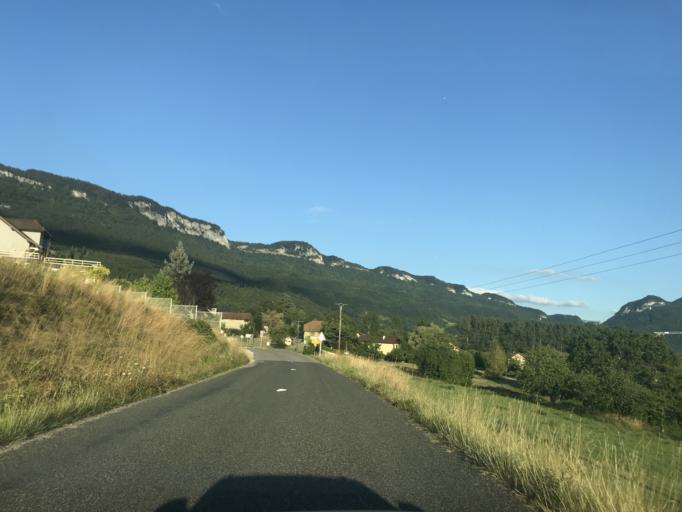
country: FR
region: Rhone-Alpes
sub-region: Departement de la Savoie
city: Yenne
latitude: 45.7199
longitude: 5.8056
